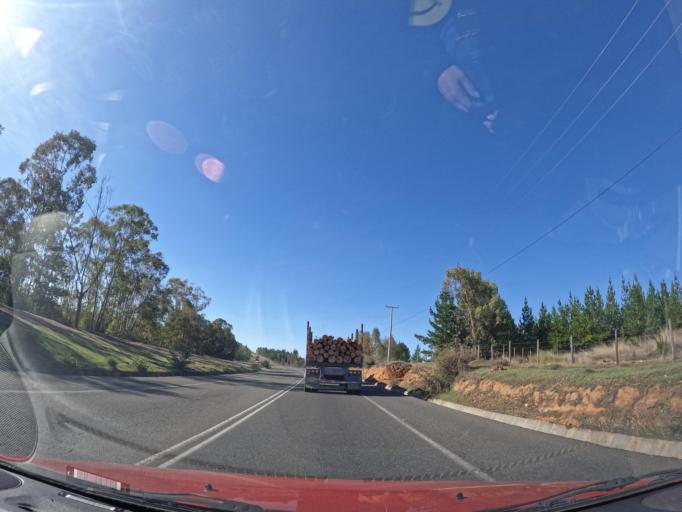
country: CL
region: Maule
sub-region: Provincia de Cauquenes
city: Cauquenes
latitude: -35.9315
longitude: -72.1909
